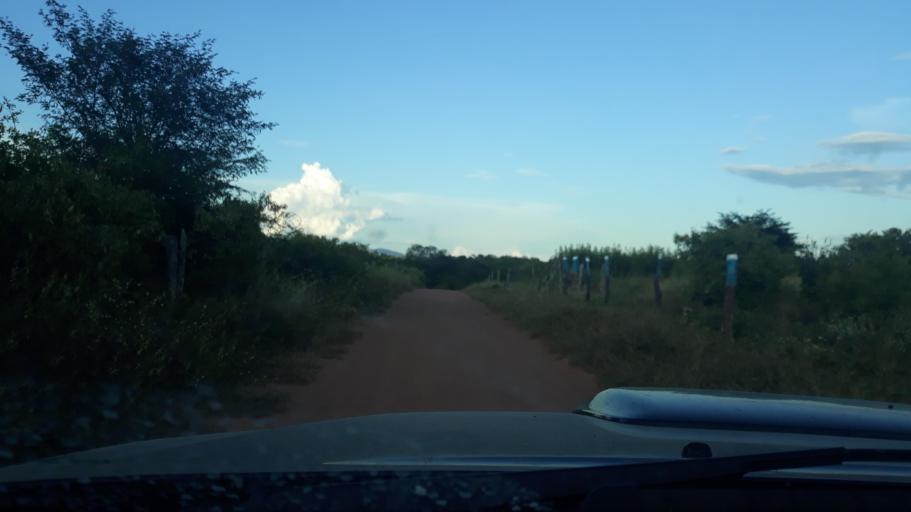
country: BR
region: Bahia
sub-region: Riacho De Santana
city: Riacho de Santana
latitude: -13.8580
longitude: -43.0642
